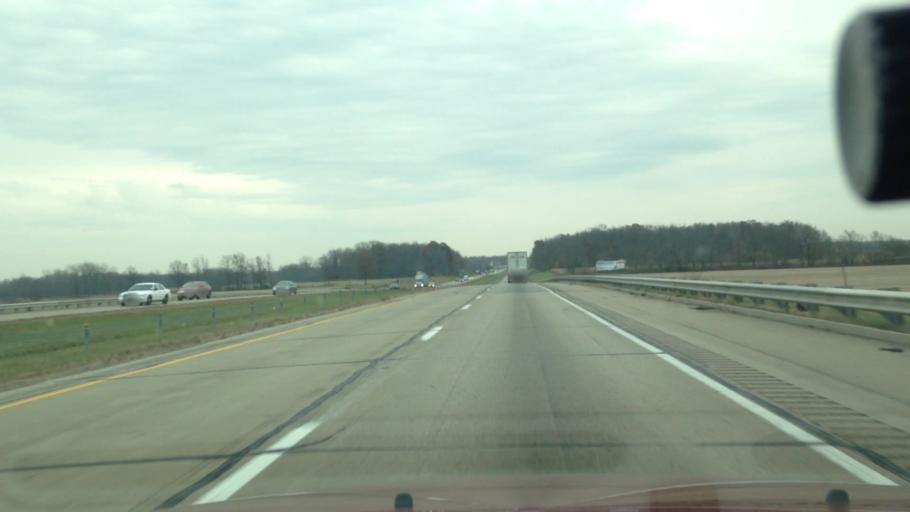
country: US
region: Indiana
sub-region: Wayne County
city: Cambridge City
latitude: 39.8525
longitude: -85.2446
